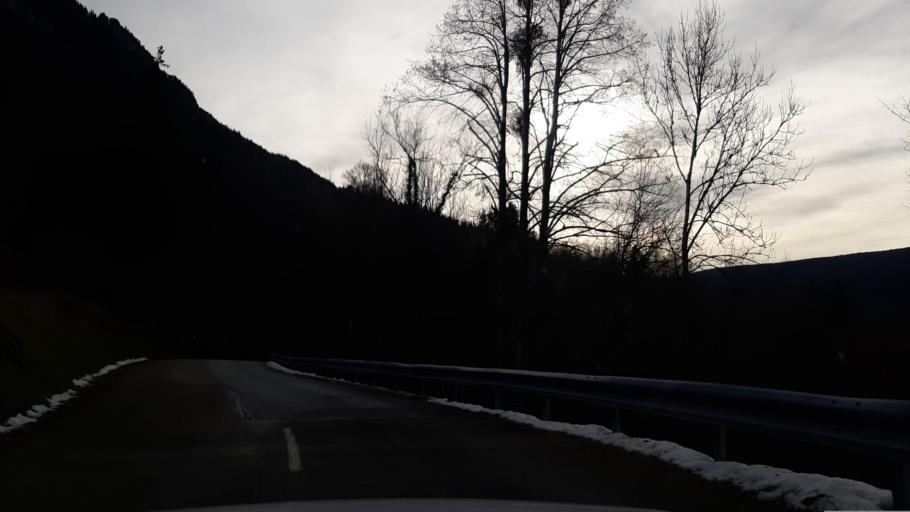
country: FR
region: Rhone-Alpes
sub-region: Departement de la Haute-Savoie
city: Cusy
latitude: 45.6690
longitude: 6.1023
